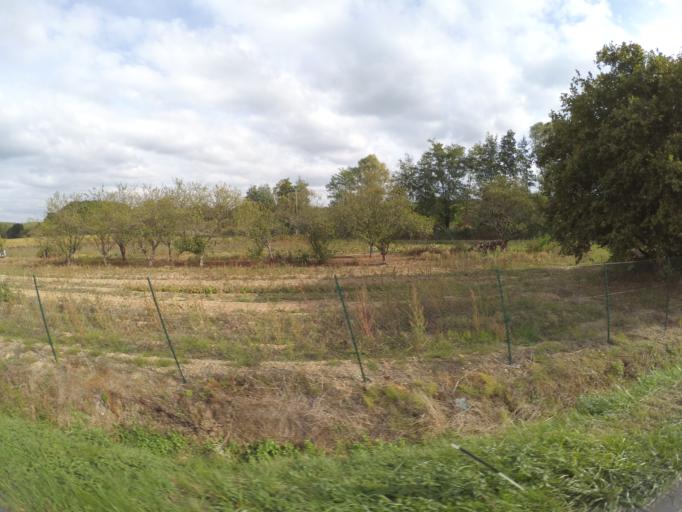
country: FR
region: Centre
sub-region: Departement d'Indre-et-Loire
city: Vernou-sur-Brenne
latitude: 47.4348
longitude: 0.8538
